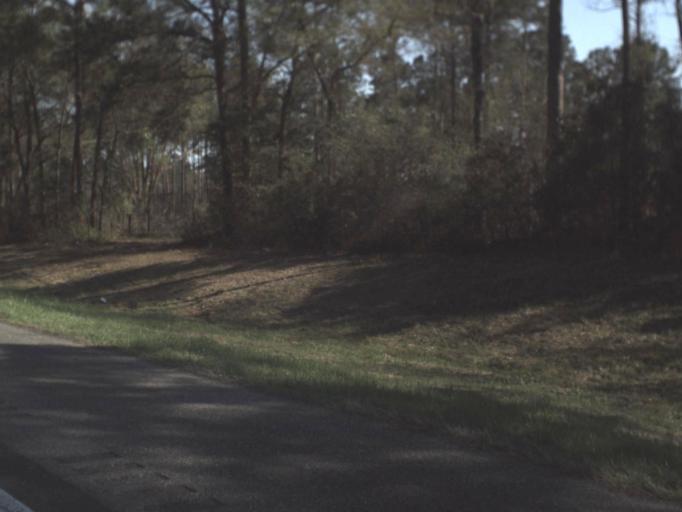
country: US
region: Florida
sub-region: Gadsden County
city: Gretna
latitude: 30.5694
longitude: -84.6702
